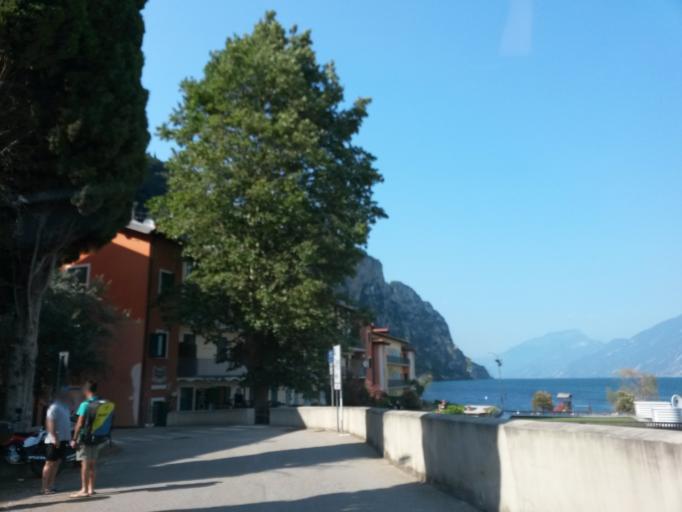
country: IT
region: Lombardy
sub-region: Provincia di Brescia
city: Pieve
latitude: 45.7545
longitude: 10.7506
